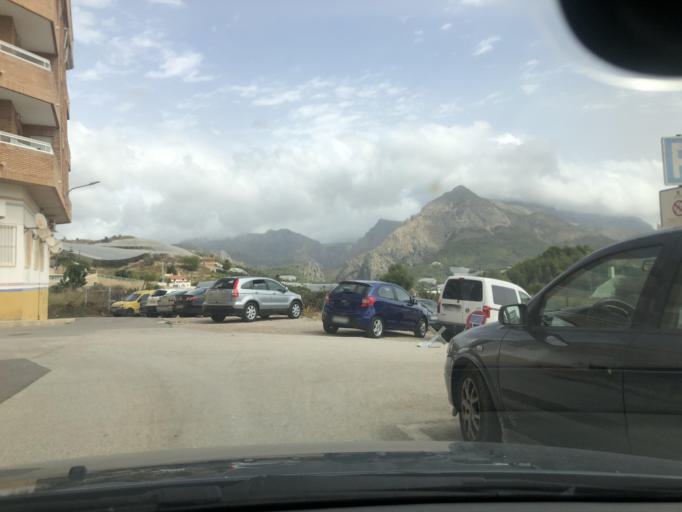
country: ES
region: Valencia
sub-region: Provincia de Alicante
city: Callosa d'En Sarria
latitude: 38.6496
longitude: -0.1192
